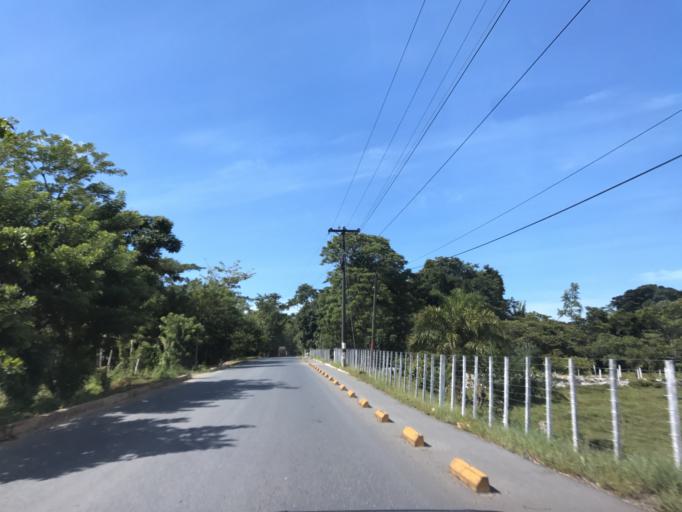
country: GT
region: Izabal
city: Morales
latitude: 15.6558
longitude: -89.0086
